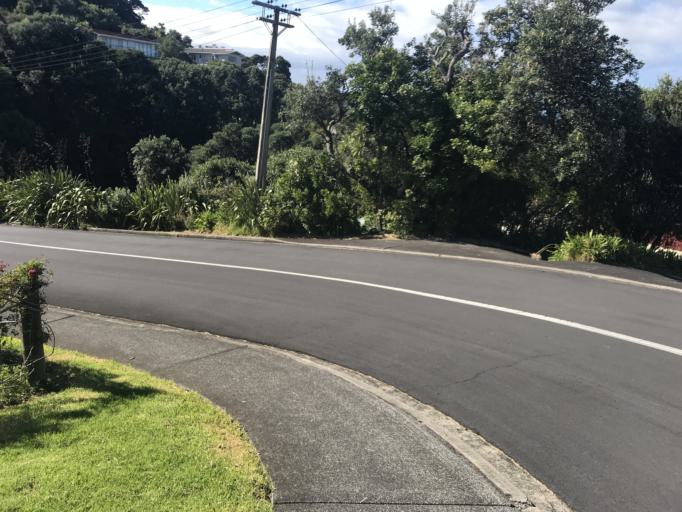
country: NZ
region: Auckland
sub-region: Auckland
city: Warkworth
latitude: -36.2997
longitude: 174.7986
